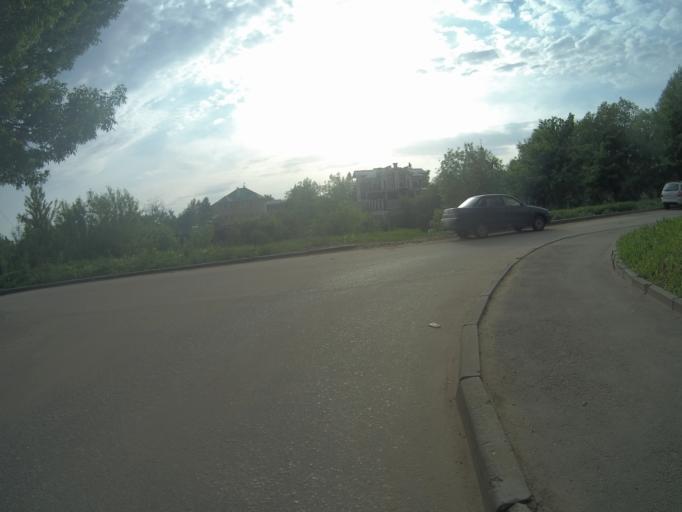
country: RU
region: Vladimir
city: Kommunar
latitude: 56.1615
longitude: 40.4494
